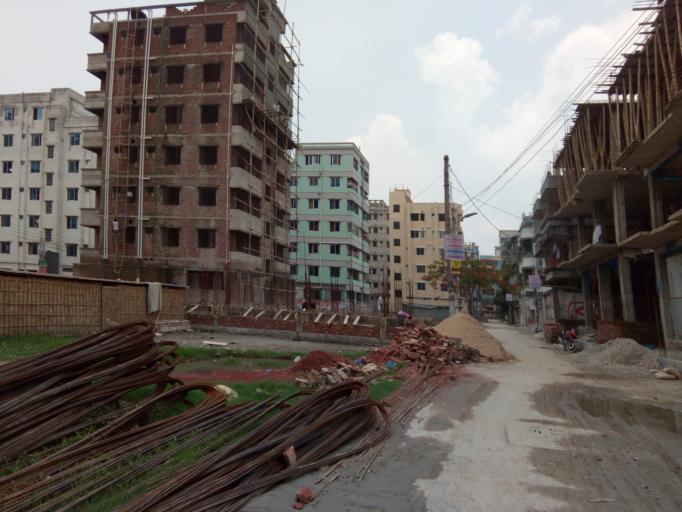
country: BD
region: Dhaka
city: Paltan
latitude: 23.7532
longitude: 90.4386
